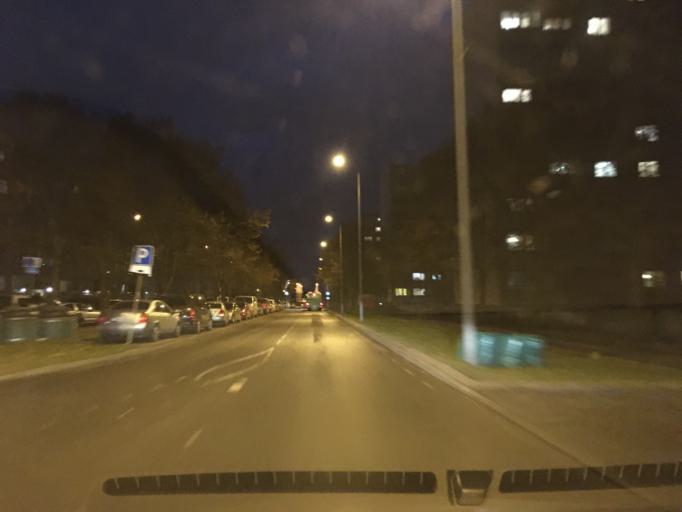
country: EE
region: Harju
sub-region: Tallinna linn
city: Kose
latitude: 59.4374
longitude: 24.8189
